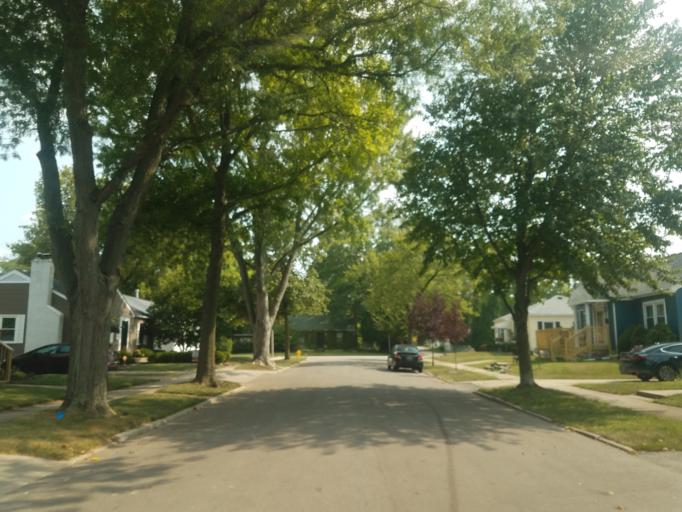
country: US
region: Illinois
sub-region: McLean County
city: Bloomington
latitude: 40.4716
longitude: -88.9707
